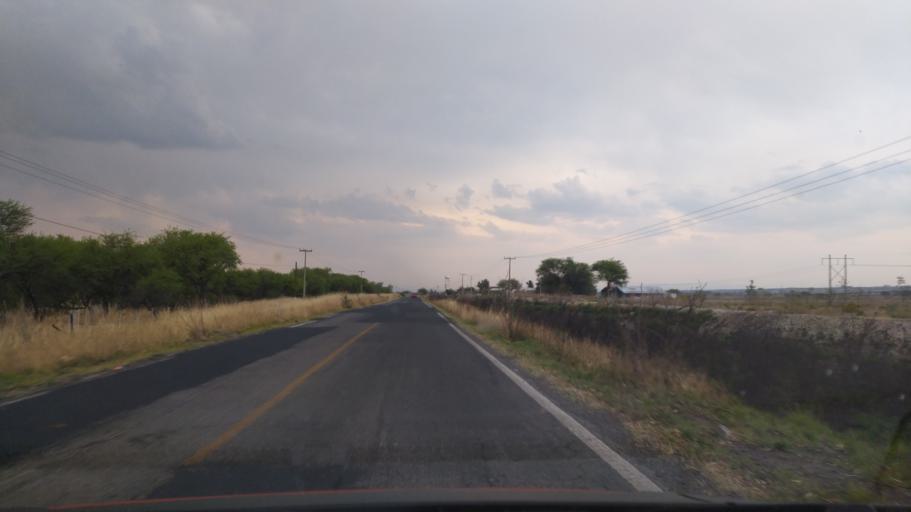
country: MX
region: Guanajuato
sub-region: San Francisco del Rincon
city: San Ignacio de Hidalgo
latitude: 20.8404
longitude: -101.8977
